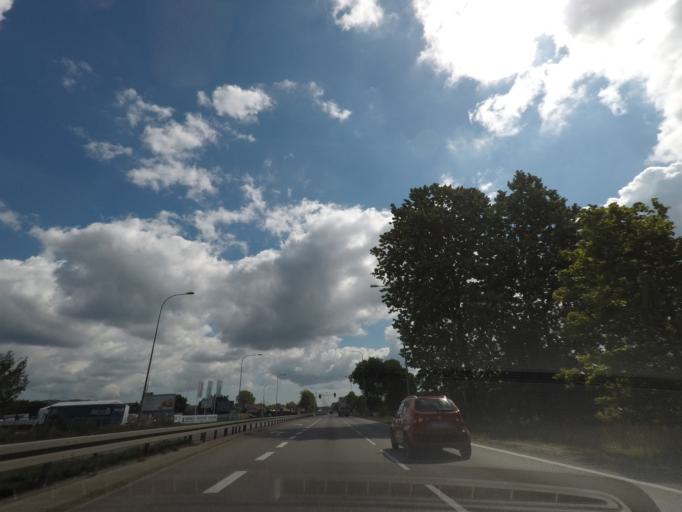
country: PL
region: Pomeranian Voivodeship
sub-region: Powiat wejherowski
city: Bolszewo
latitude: 54.6096
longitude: 18.1976
